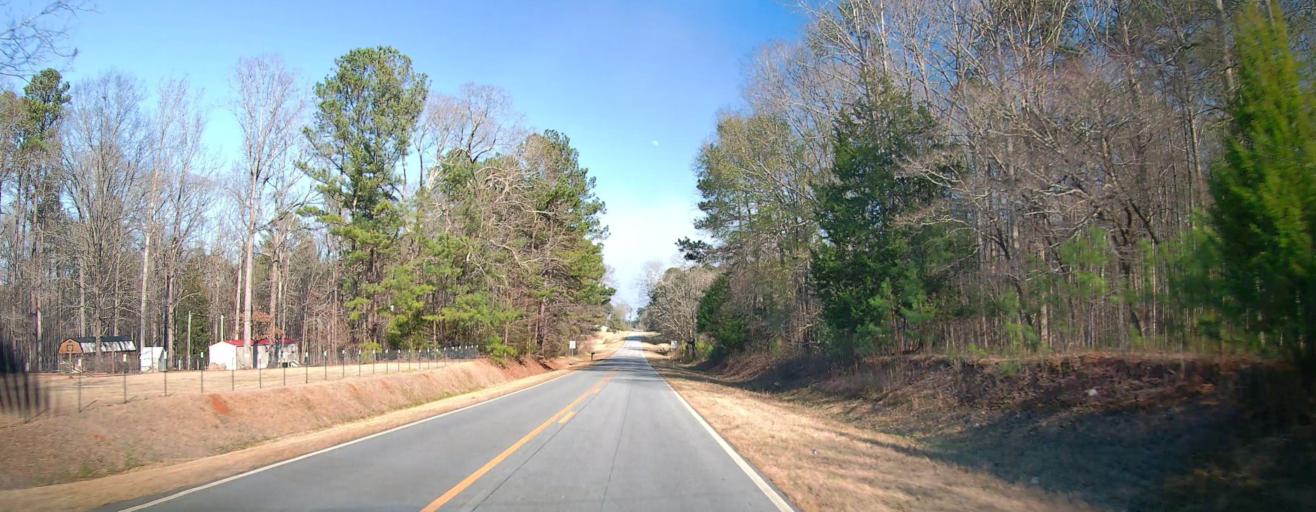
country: US
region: Georgia
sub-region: Monroe County
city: Forsyth
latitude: 33.1014
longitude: -83.8265
